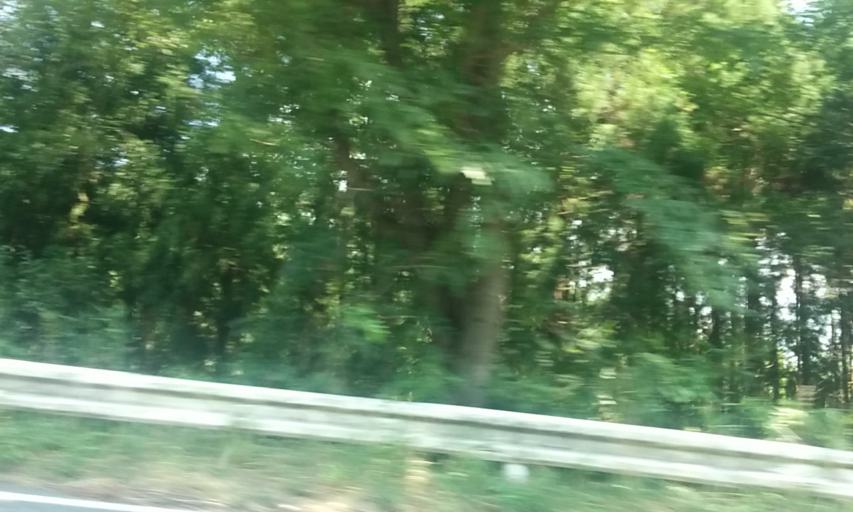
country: JP
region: Kyoto
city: Fukuchiyama
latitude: 35.2617
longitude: 135.1467
